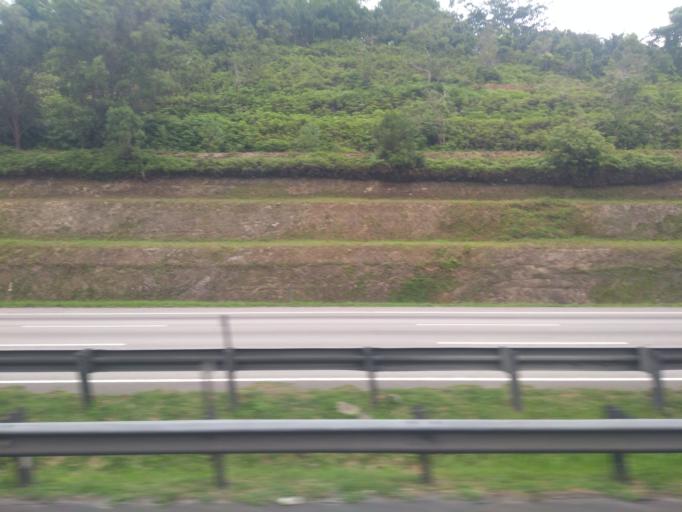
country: MY
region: Negeri Sembilan
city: Tampin
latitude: 2.4659
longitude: 102.1542
